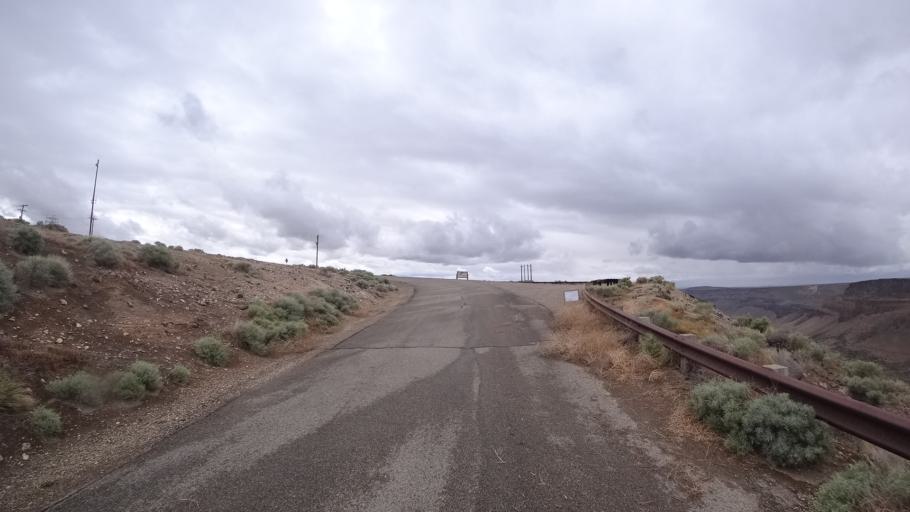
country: US
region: Idaho
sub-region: Owyhee County
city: Murphy
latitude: 43.2386
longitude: -116.3683
